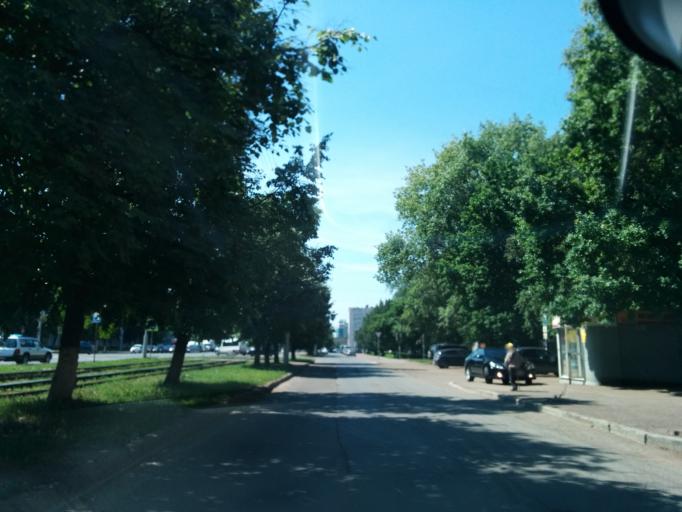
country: RU
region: Bashkortostan
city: Ufa
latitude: 54.7530
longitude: 55.9892
